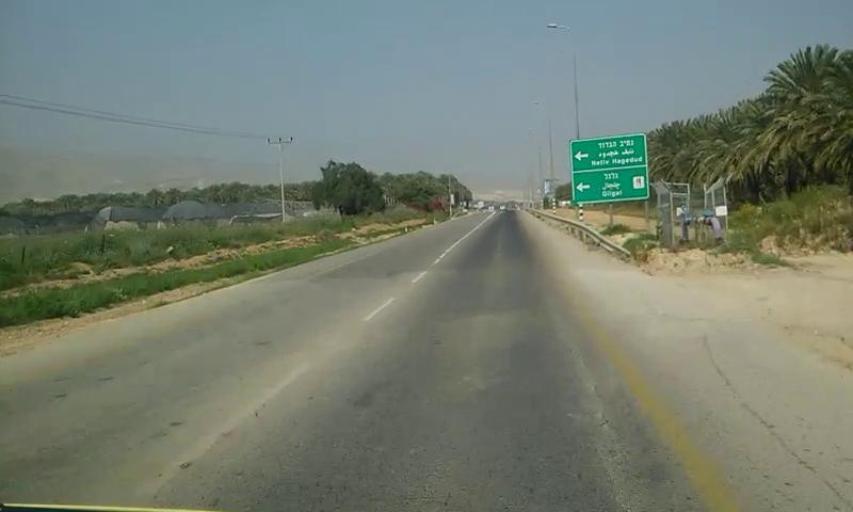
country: PS
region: West Bank
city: Al Fasayil
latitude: 31.9978
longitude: 35.4552
